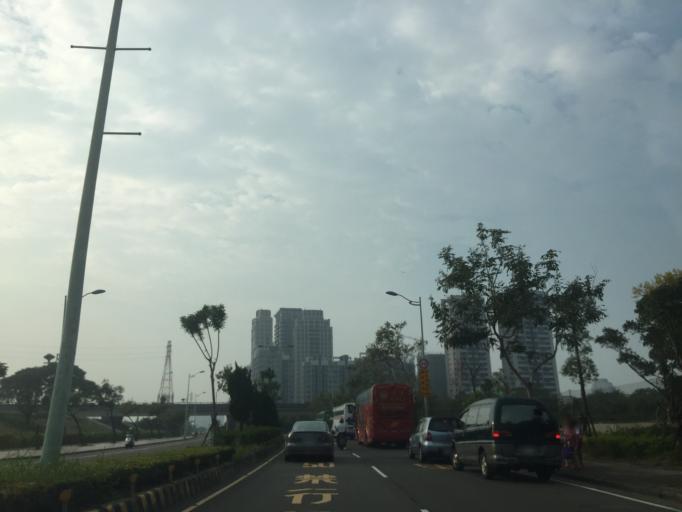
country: TW
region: Taiwan
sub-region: Hsinchu
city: Zhubei
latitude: 24.8157
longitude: 121.0147
